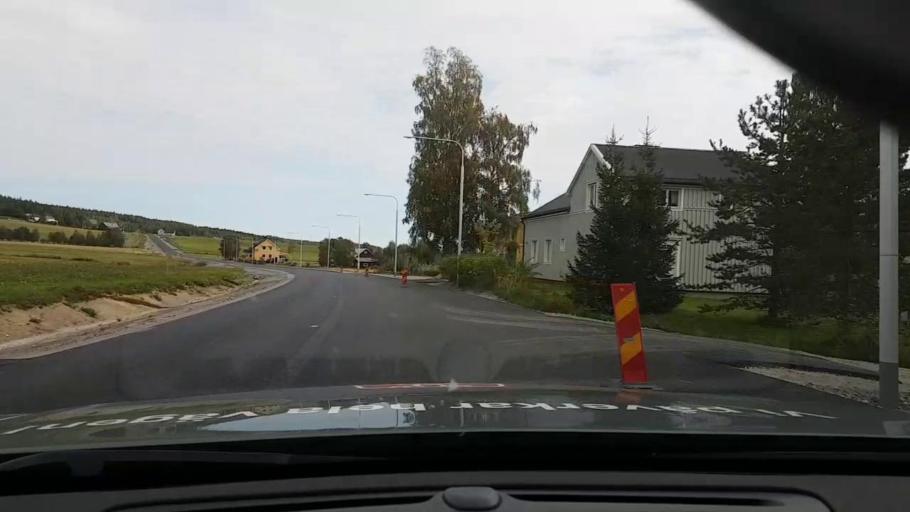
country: SE
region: Vaesternorrland
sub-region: OErnskoeldsviks Kommun
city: Bjasta
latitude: 63.2889
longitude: 18.4506
